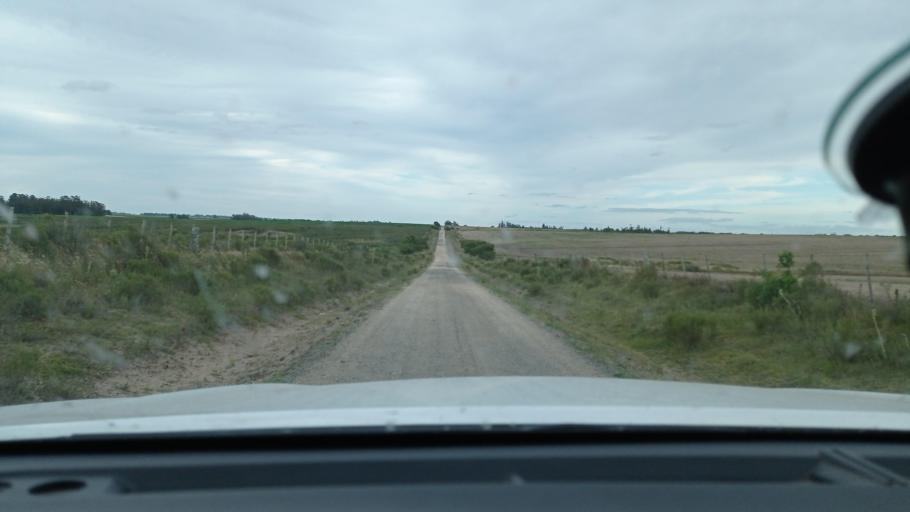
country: UY
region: Florida
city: Casupa
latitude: -34.1407
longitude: -55.7864
